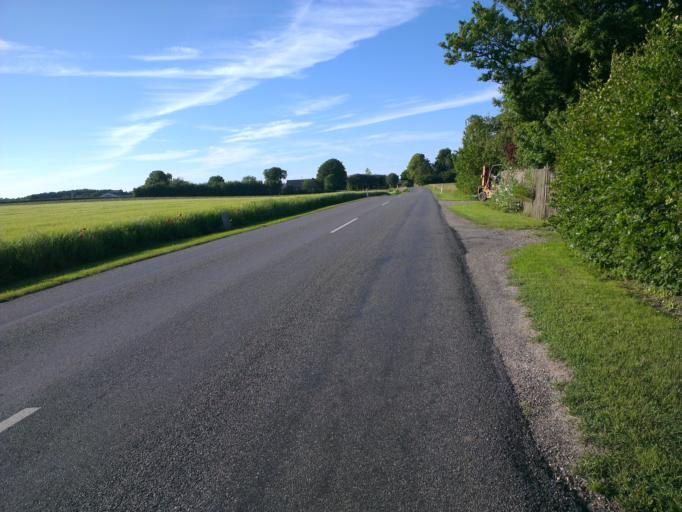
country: DK
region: Capital Region
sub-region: Frederikssund Kommune
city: Frederikssund
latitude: 55.8065
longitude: 12.0228
